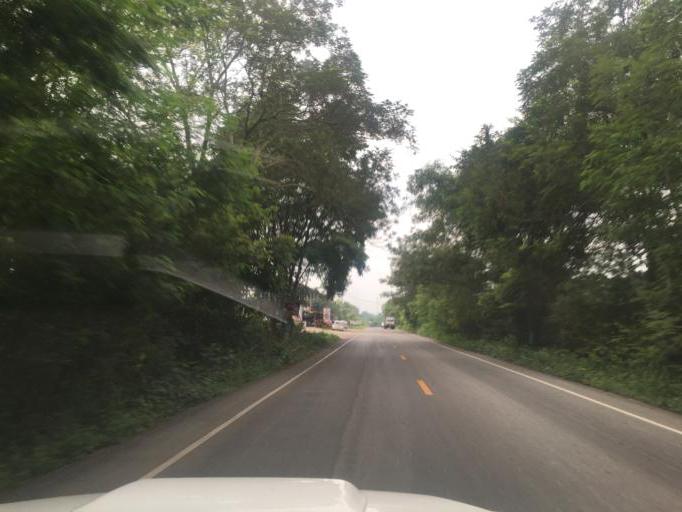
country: TH
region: Changwat Udon Thani
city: Udon Thani
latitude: 17.3343
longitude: 102.7153
